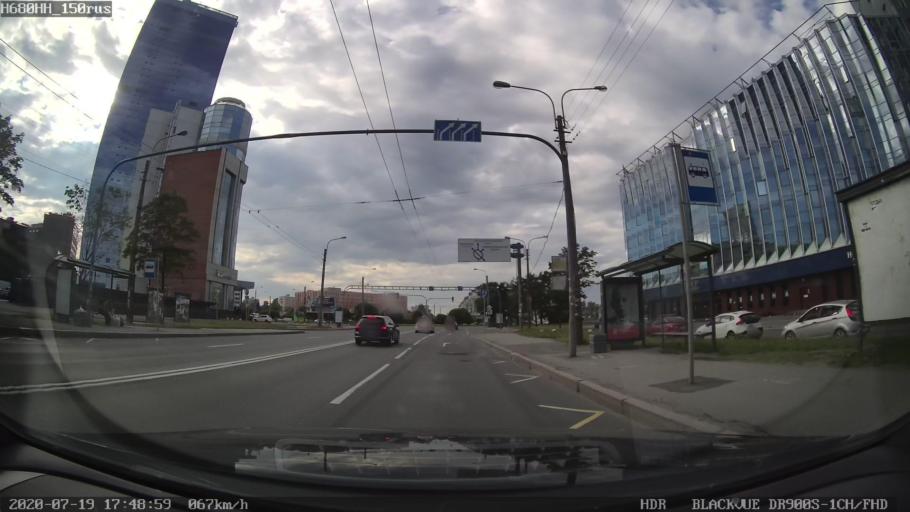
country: RU
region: St.-Petersburg
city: Avtovo
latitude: 59.8504
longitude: 30.3079
